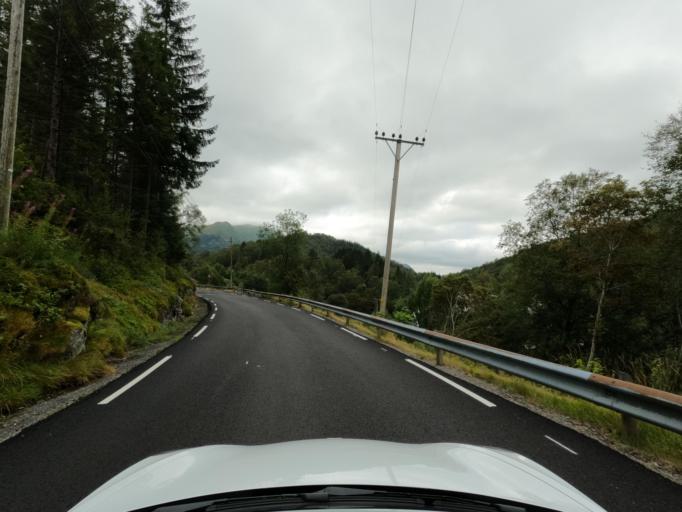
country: NO
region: Hordaland
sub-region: Bergen
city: Espeland
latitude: 60.3747
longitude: 5.4942
